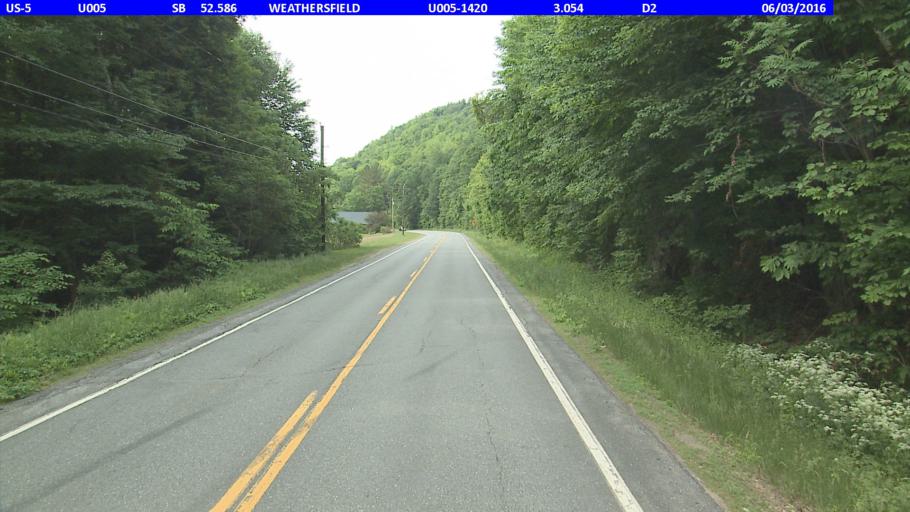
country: US
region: New Hampshire
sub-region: Sullivan County
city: Claremont
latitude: 43.3792
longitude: -72.4170
